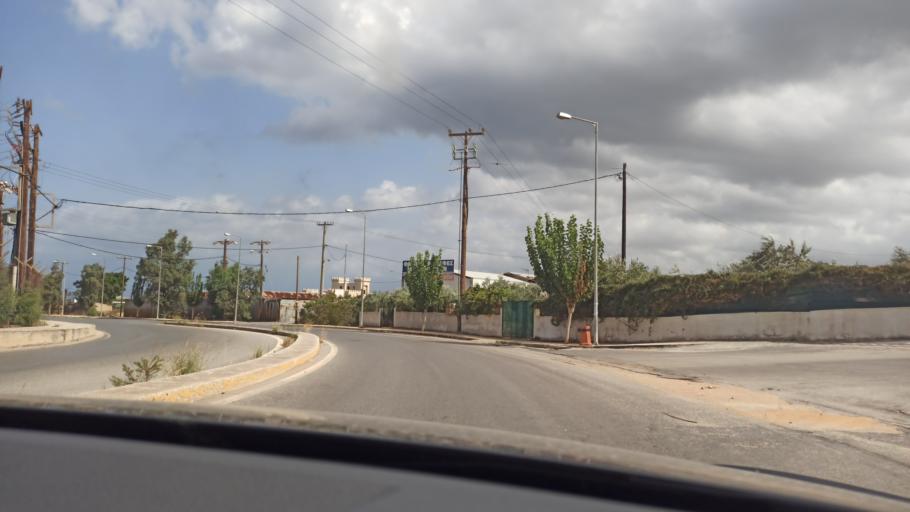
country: GR
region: Crete
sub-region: Nomos Irakleiou
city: Gazi
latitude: 35.3386
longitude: 25.0513
